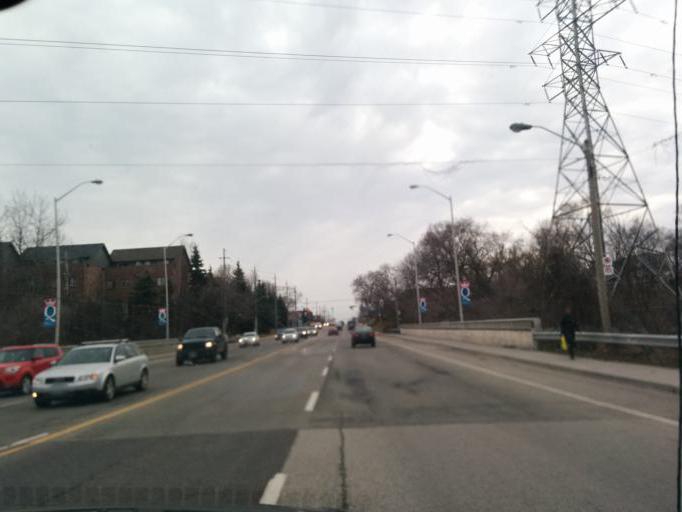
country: CA
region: Ontario
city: Etobicoke
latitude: 43.6287
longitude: -79.4922
